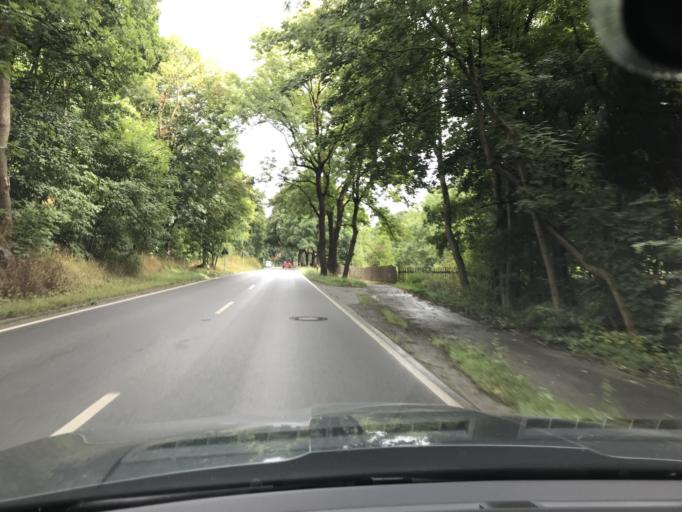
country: DE
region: Saxony-Anhalt
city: Elbingerode
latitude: 51.7685
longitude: 10.8142
